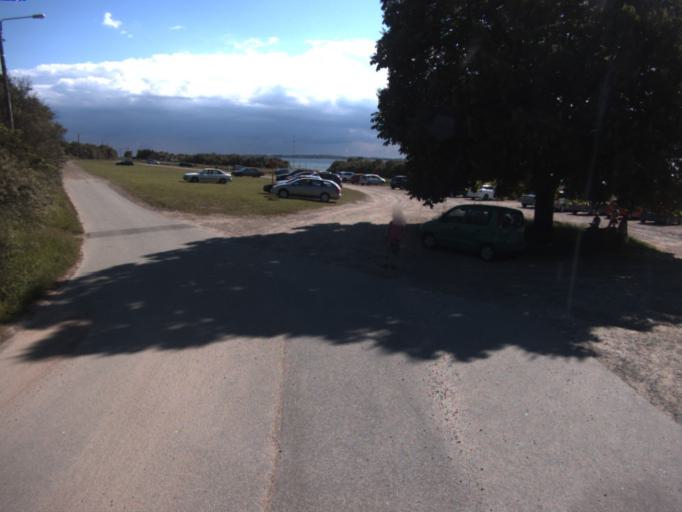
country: SE
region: Skane
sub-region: Helsingborg
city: Rydeback
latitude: 55.9674
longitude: 12.7592
